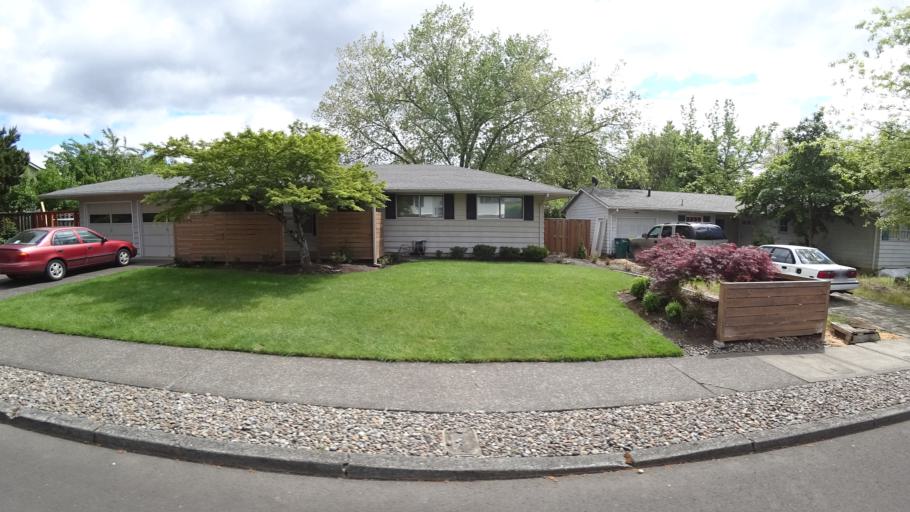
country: US
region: Oregon
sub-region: Washington County
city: Beaverton
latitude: 45.4659
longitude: -122.8016
